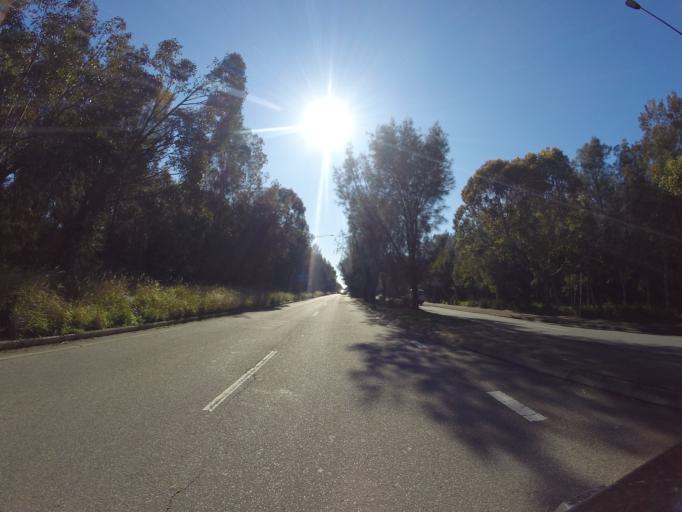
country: AU
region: New South Wales
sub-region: Auburn
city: Auburn
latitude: -33.8442
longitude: 151.0574
